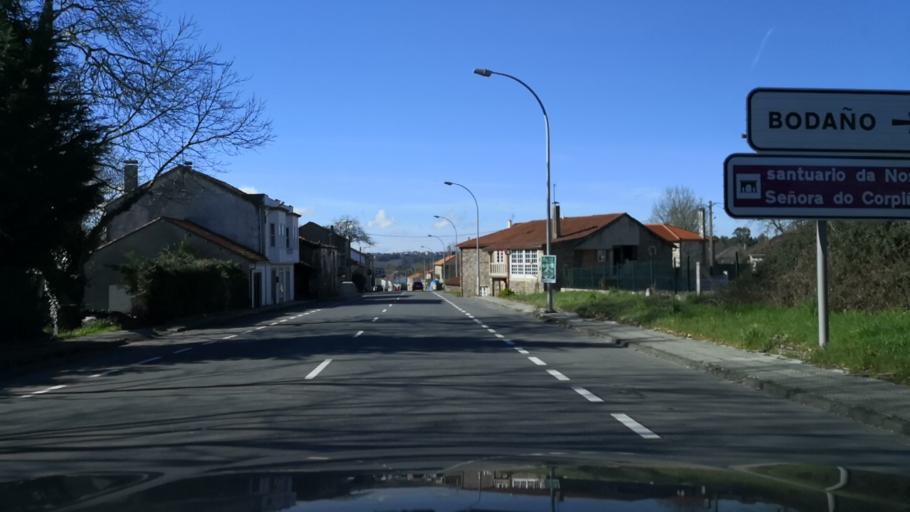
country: ES
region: Galicia
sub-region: Provincia de Pontevedra
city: Silleda
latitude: 42.6828
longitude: -8.1827
